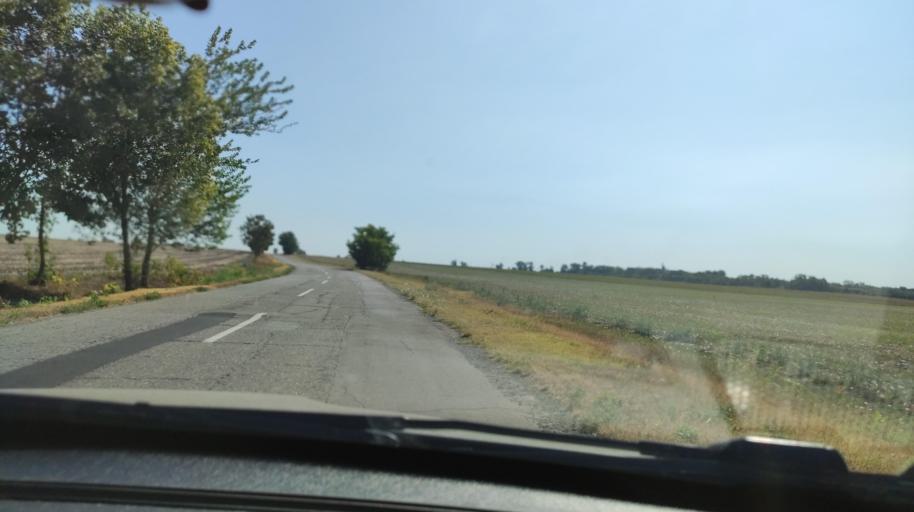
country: RS
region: Autonomna Pokrajina Vojvodina
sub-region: Severnobacki Okrug
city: Backa Topola
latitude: 45.8672
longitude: 19.6208
